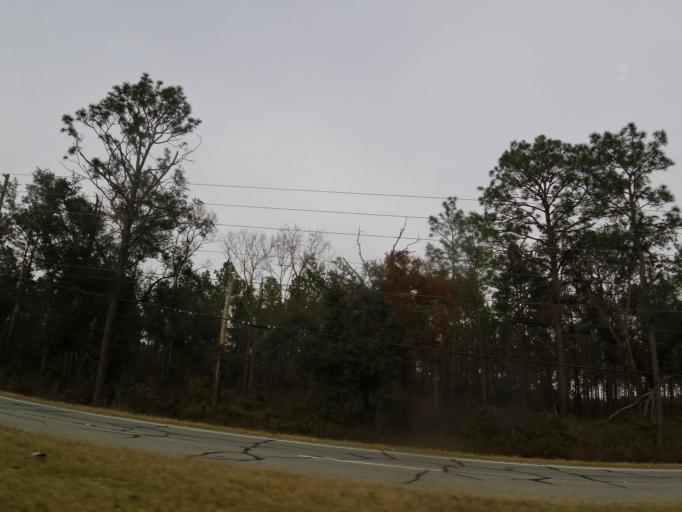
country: US
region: Georgia
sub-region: Decatur County
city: Bainbridge
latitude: 30.9307
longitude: -84.6349
